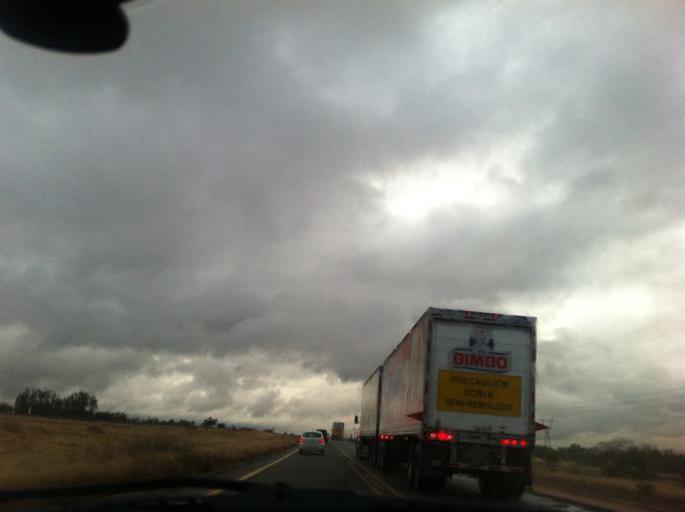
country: MX
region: Sonora
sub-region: San Miguel de Horcasitas
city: Las Mercedes [Agropecuaria]
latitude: 29.6213
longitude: -111.0284
